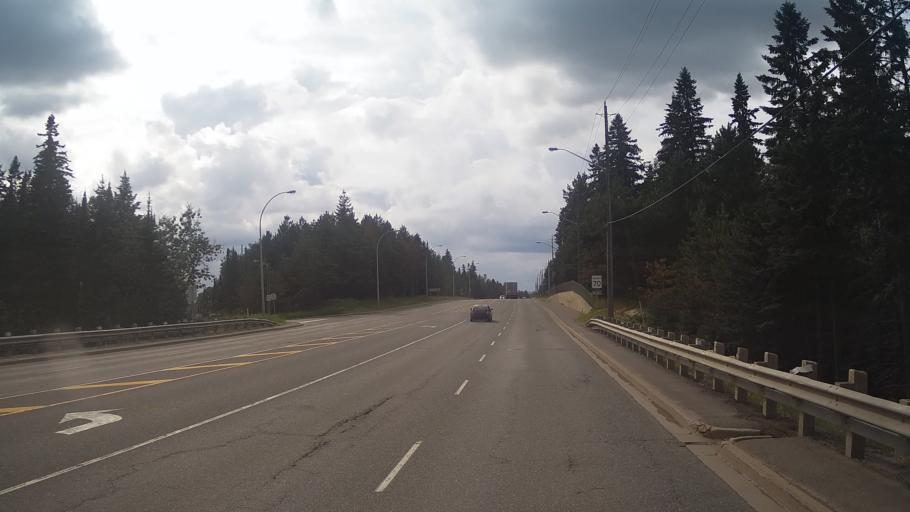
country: CA
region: Ontario
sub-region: Thunder Bay District
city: Thunder Bay
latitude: 48.4605
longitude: -89.2716
